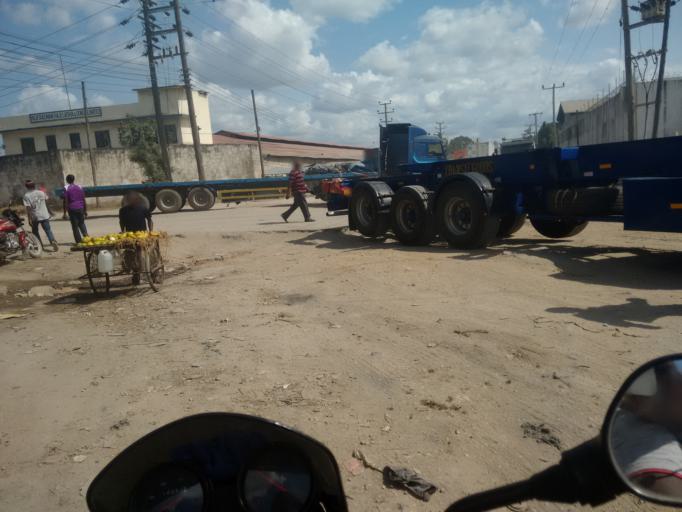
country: TZ
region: Dar es Salaam
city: Dar es Salaam
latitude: -6.8462
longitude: 39.2574
